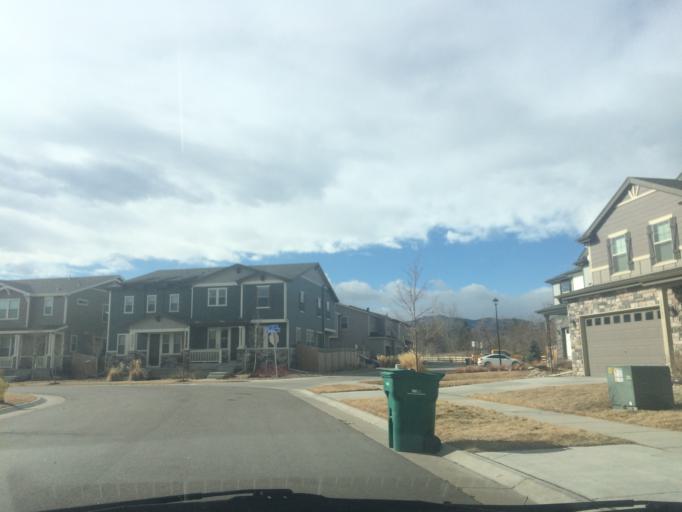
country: US
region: Colorado
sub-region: Jefferson County
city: Applewood
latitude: 39.8244
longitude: -105.1711
